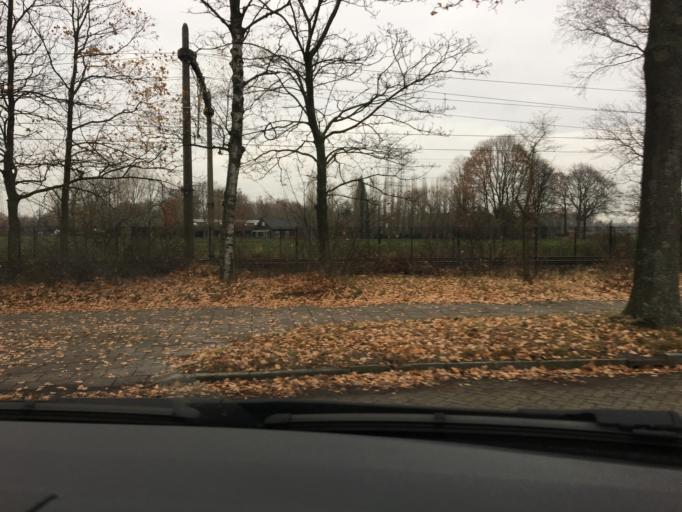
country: NL
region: North Brabant
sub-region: Gemeente Eindhoven
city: Muschberg en Geestenberg
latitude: 51.4480
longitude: 5.5300
